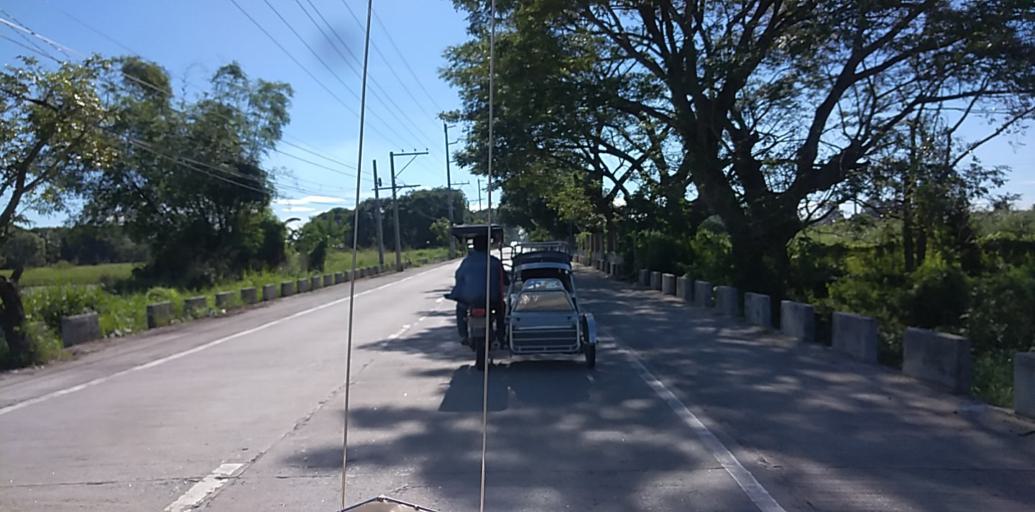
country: PH
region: Central Luzon
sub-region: Province of Pampanga
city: Santo Domingo
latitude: 15.0687
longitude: 120.7651
